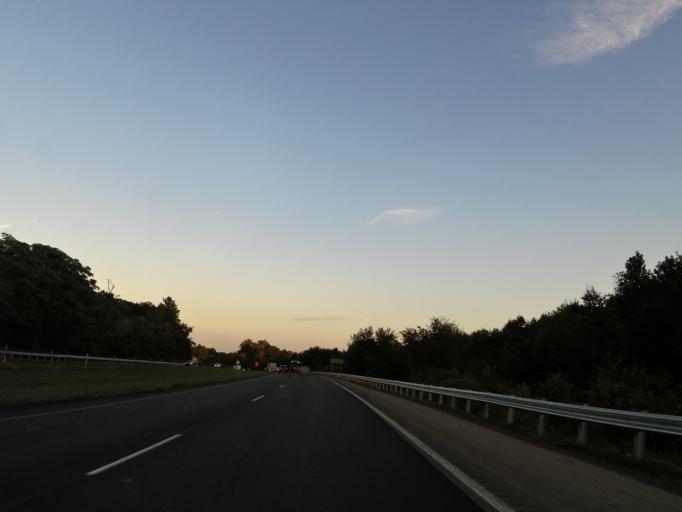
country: US
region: Tennessee
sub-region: Roane County
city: Kingston
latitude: 35.8739
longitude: -84.4989
